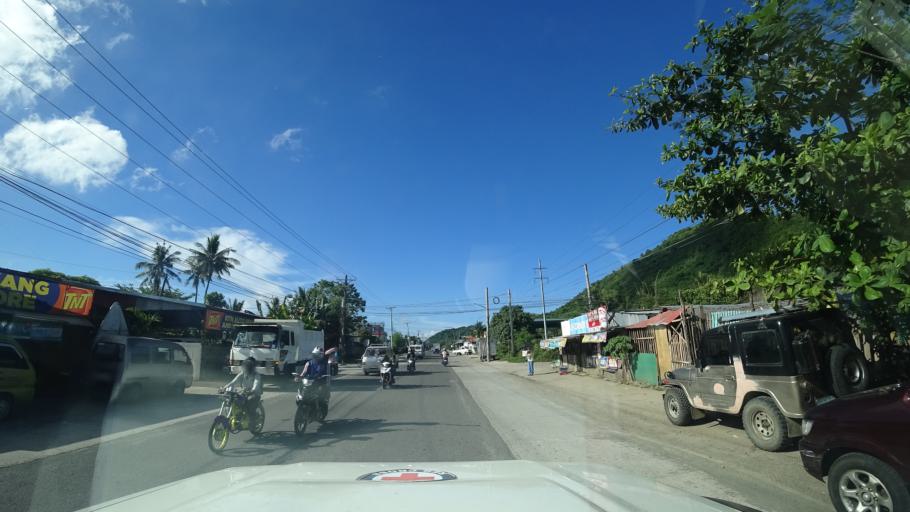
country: PH
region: Eastern Visayas
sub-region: Province of Leyte
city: Pawing
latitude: 11.2056
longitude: 124.9914
